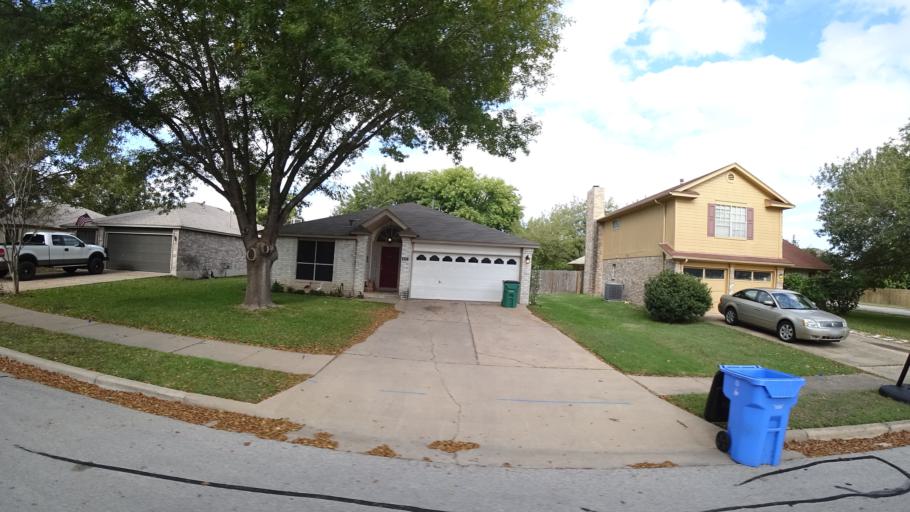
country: US
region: Texas
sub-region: Travis County
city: Pflugerville
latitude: 30.4371
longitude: -97.6283
